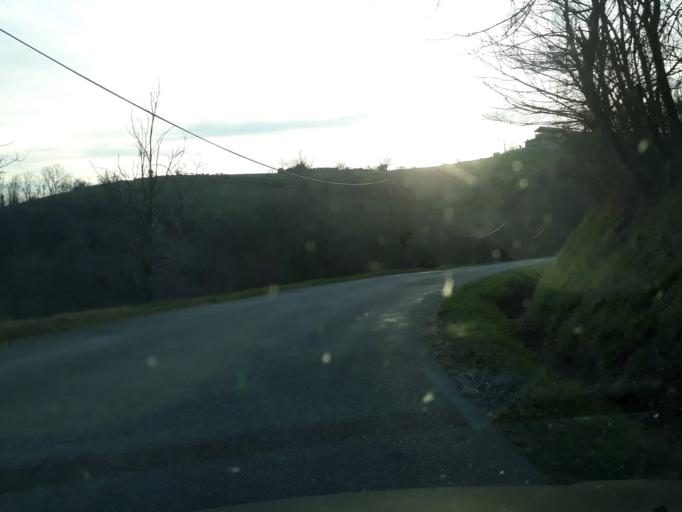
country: FR
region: Midi-Pyrenees
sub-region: Departement de la Haute-Garonne
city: Montesquieu-Volvestre
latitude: 43.1727
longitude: 1.3224
